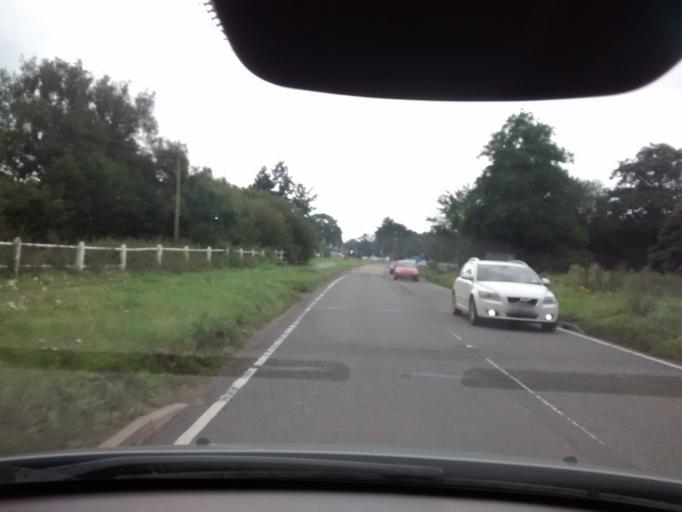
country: GB
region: England
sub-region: Hampshire
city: Ringwood
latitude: 50.8562
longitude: -1.7881
